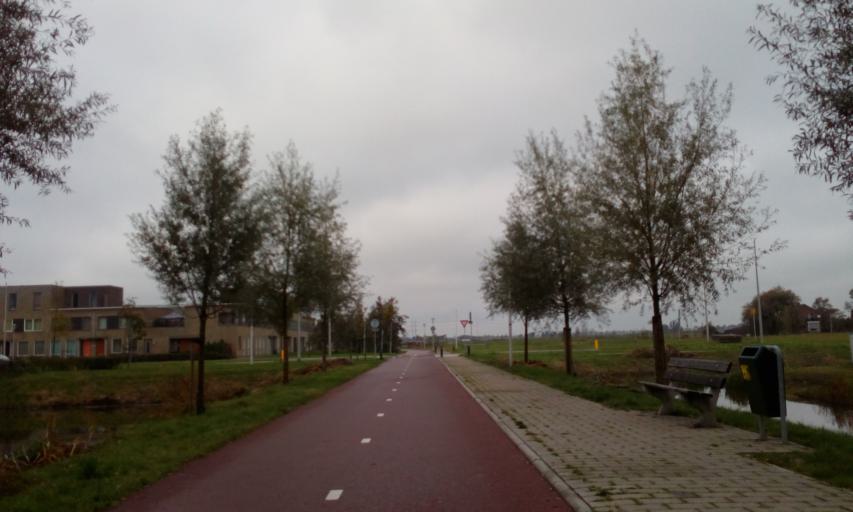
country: NL
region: South Holland
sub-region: Gemeente Lansingerland
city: Berkel en Rodenrijs
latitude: 52.0011
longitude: 4.4696
